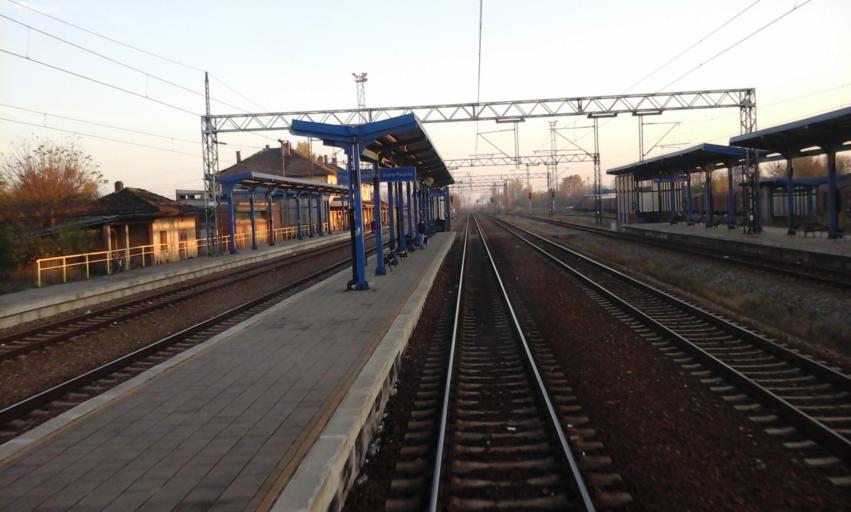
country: RS
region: Autonomna Pokrajina Vojvodina
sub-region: Sremski Okrug
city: Stara Pazova
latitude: 44.9866
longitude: 20.1375
